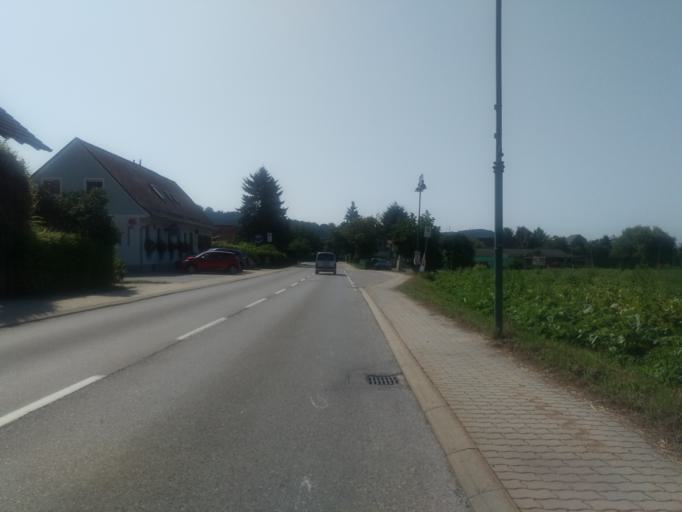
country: AT
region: Styria
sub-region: Politischer Bezirk Graz-Umgebung
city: Fernitz
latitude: 46.9685
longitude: 15.5021
